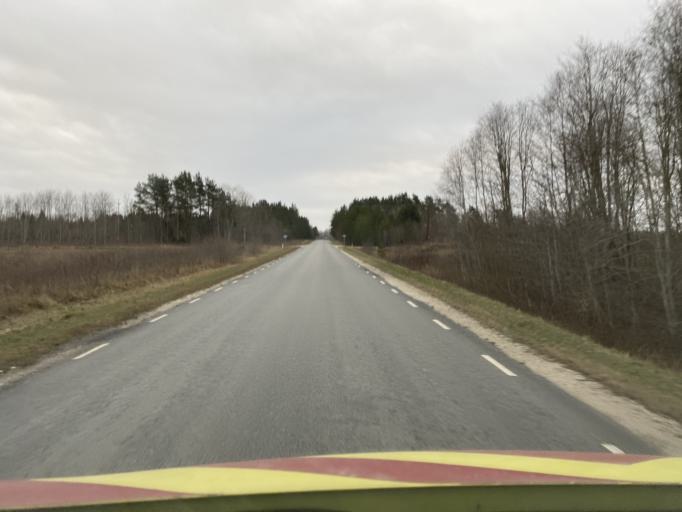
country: EE
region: Laeaene
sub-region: Ridala Parish
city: Uuemoisa
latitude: 59.0365
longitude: 23.6361
